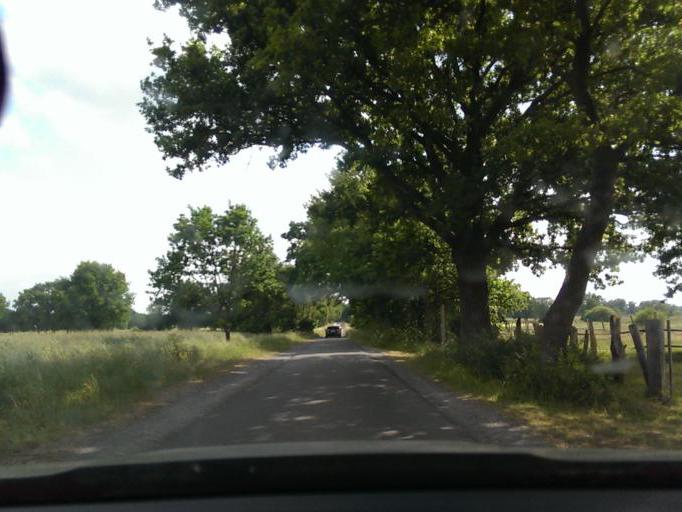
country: DE
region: Lower Saxony
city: Lindwedel
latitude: 52.5457
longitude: 9.6715
